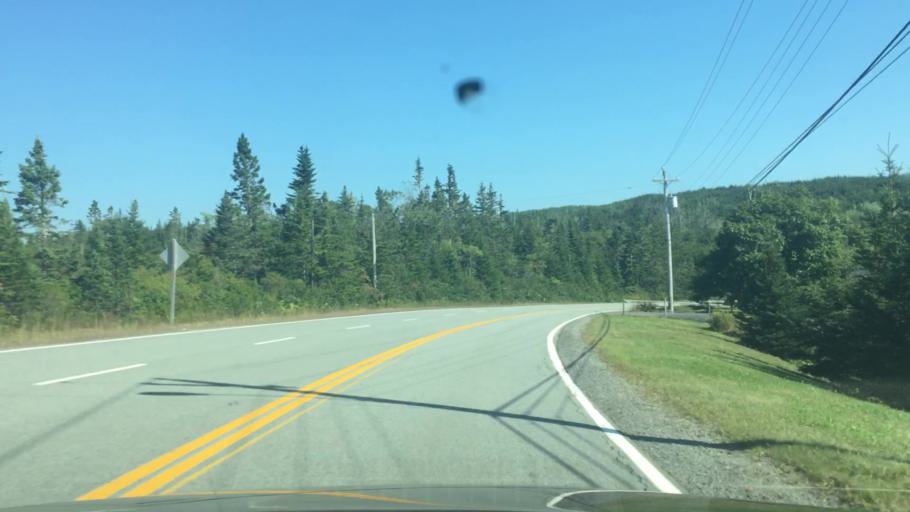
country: CA
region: Nova Scotia
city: New Glasgow
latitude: 44.8131
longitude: -62.6408
